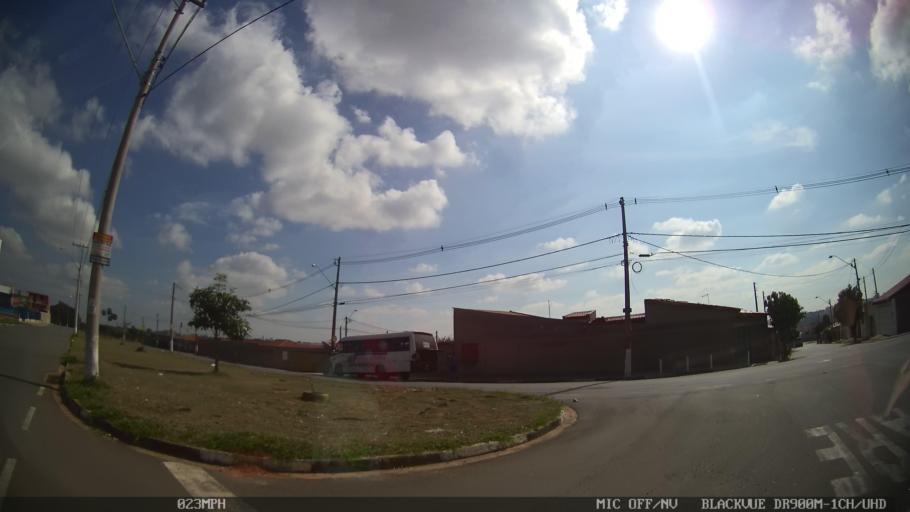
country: BR
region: Sao Paulo
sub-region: Indaiatuba
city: Indaiatuba
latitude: -22.9719
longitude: -47.1744
